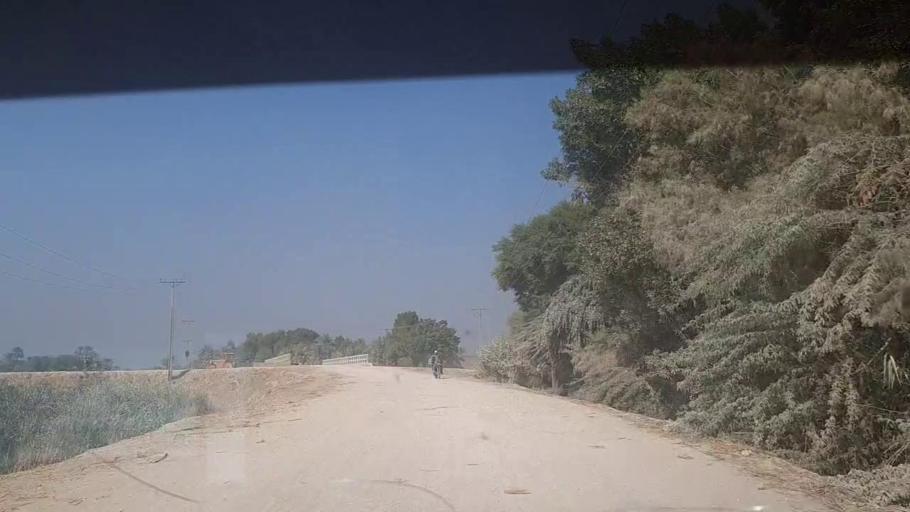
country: PK
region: Sindh
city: Kot Diji
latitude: 27.3581
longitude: 68.7102
